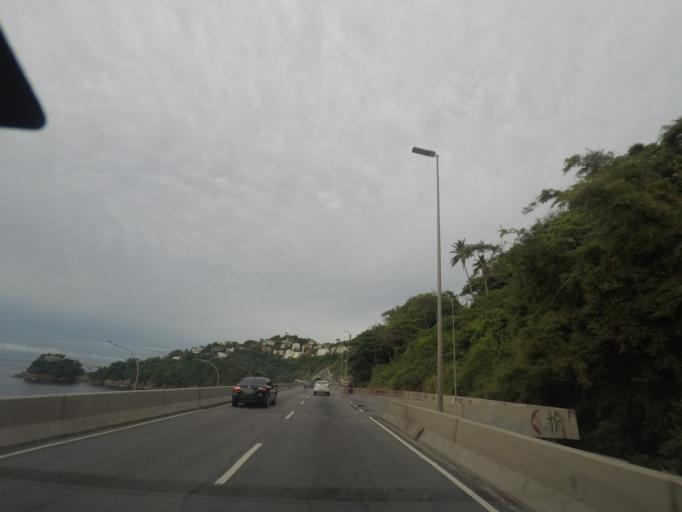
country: BR
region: Rio de Janeiro
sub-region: Rio De Janeiro
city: Rio de Janeiro
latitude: -23.0067
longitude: -43.2830
